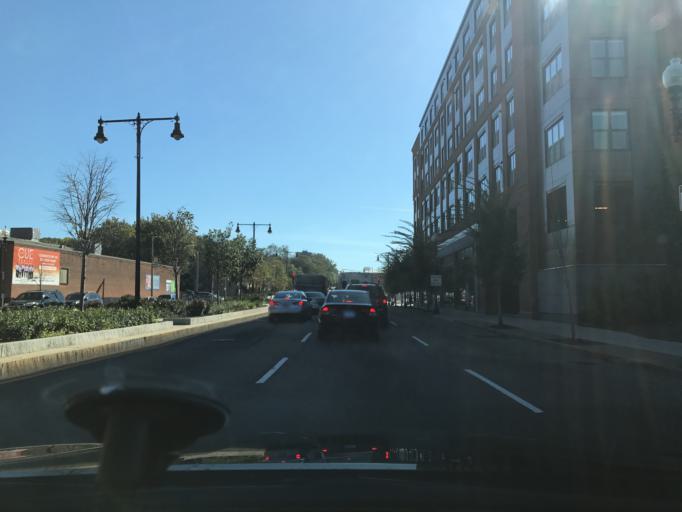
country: US
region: Massachusetts
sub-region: Norfolk County
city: Brookline
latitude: 42.3237
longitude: -71.0986
